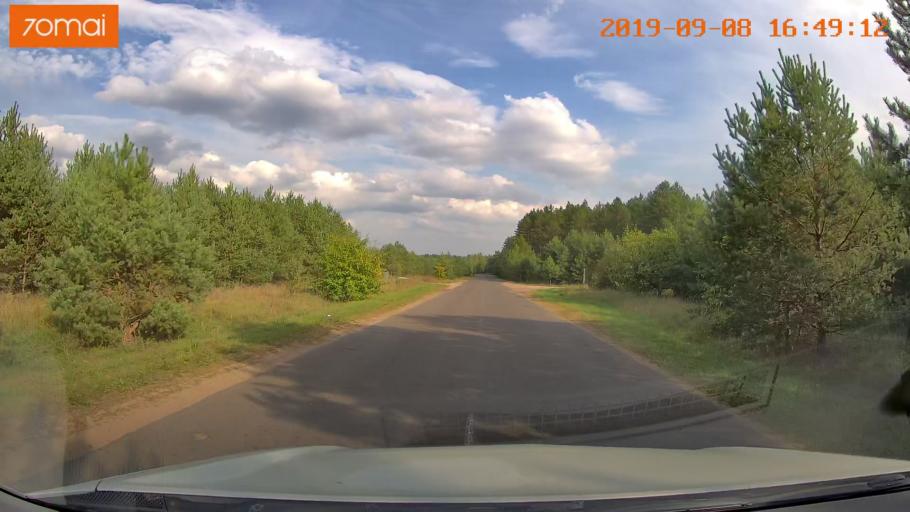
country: BY
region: Grodnenskaya
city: Hrodna
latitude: 53.8107
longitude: 23.8692
